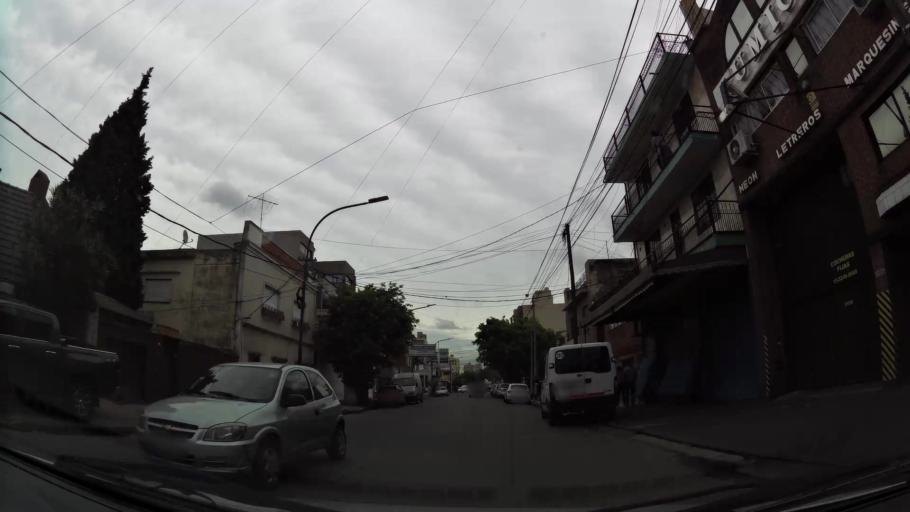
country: AR
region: Buenos Aires
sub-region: Partido de Lanus
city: Lanus
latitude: -34.7013
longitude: -58.3832
